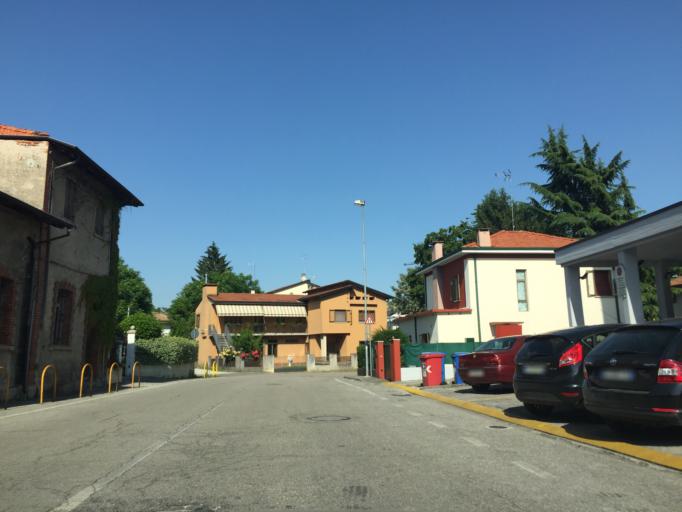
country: IT
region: Friuli Venezia Giulia
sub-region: Provincia di Pordenone
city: Porcia
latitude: 45.9637
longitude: 12.6386
